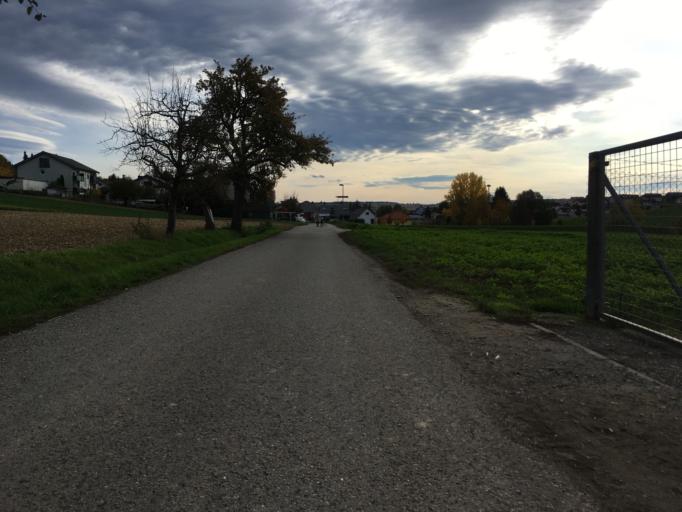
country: DE
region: Baden-Wuerttemberg
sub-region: Karlsruhe Region
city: Sinsheim
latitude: 49.2592
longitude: 8.9047
